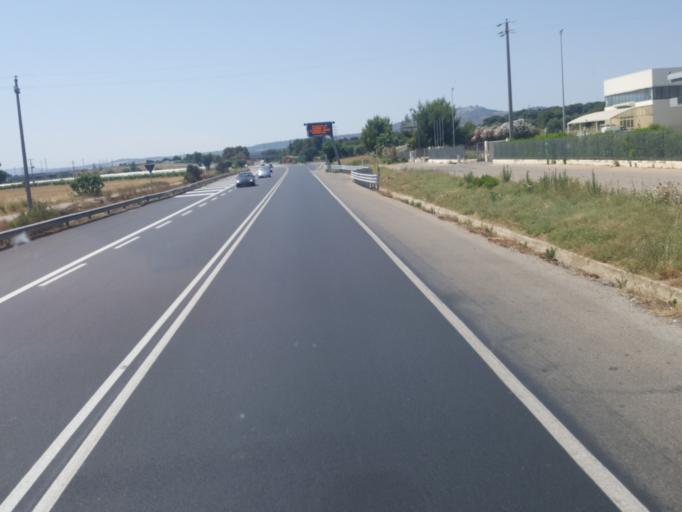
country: IT
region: Apulia
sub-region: Provincia di Taranto
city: Massafra
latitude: 40.5942
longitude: 17.0904
